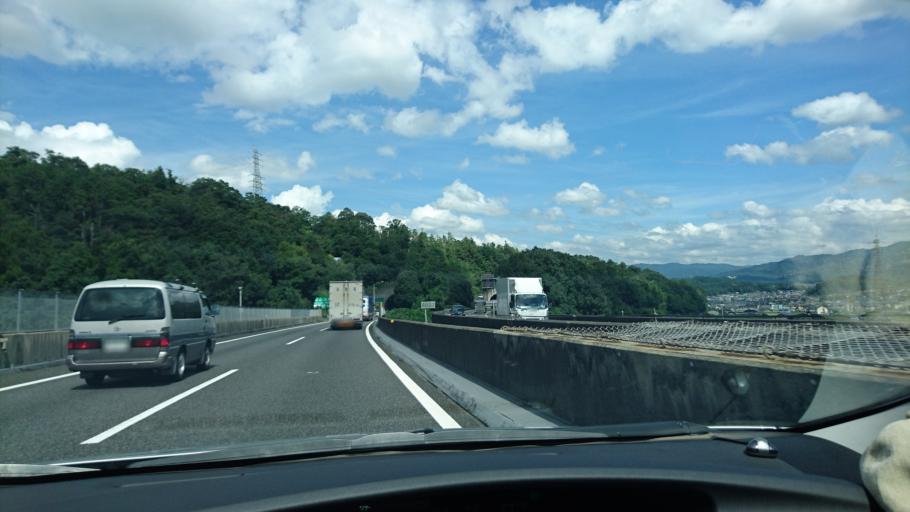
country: JP
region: Shiga Prefecture
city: Otsu-shi
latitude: 34.9469
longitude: 135.8904
